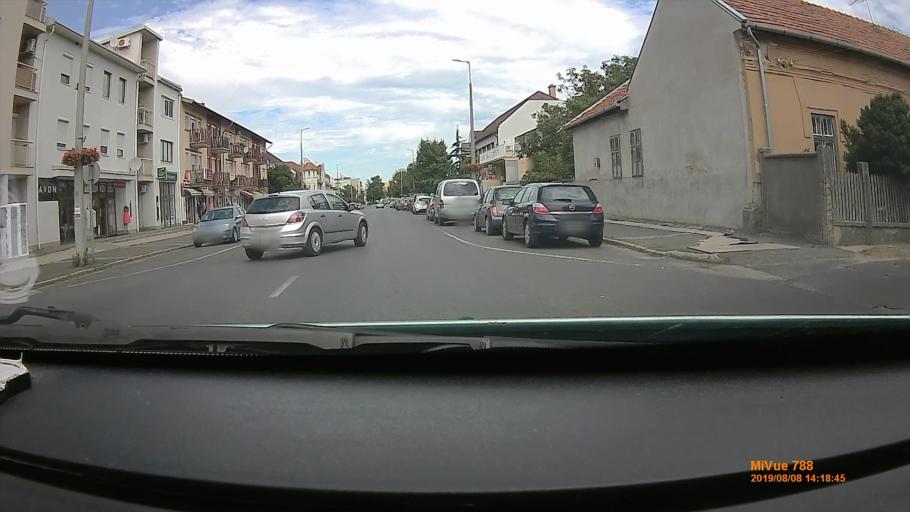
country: HU
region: Szabolcs-Szatmar-Bereg
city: Mateszalka
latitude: 47.9518
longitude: 22.3160
